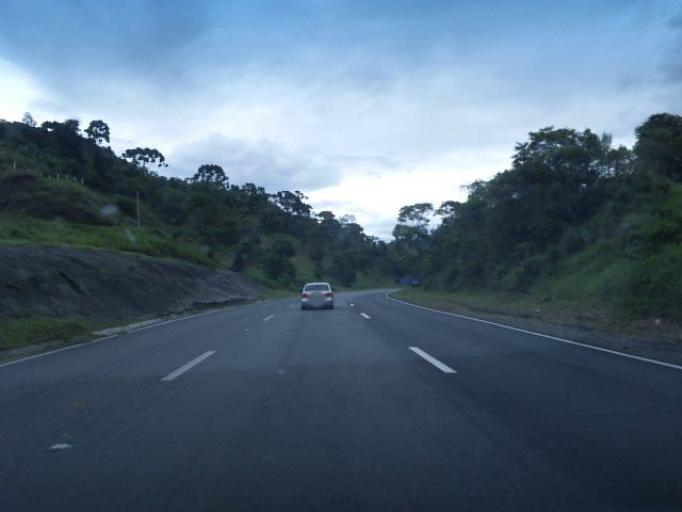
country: BR
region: Sao Paulo
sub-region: Cajati
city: Cajati
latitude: -24.9641
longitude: -48.4800
